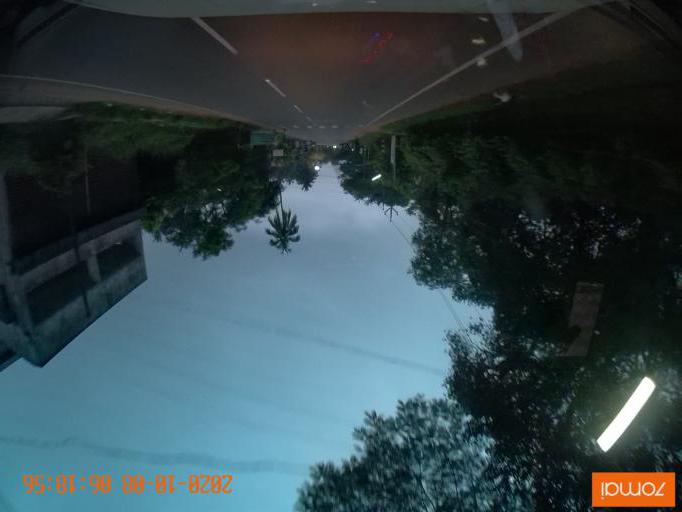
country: IN
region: Kerala
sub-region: Thrissur District
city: Trichur
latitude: 10.5145
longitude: 76.2425
